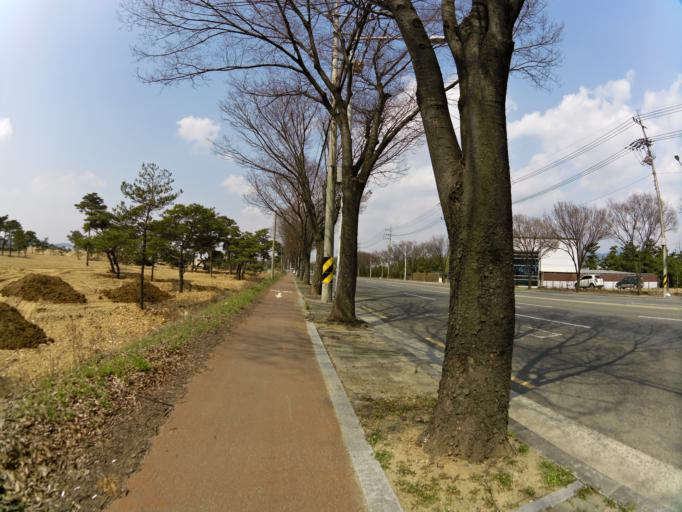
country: KR
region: Gyeongsangbuk-do
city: Gyeongsan-si
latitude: 35.8565
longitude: 128.7211
